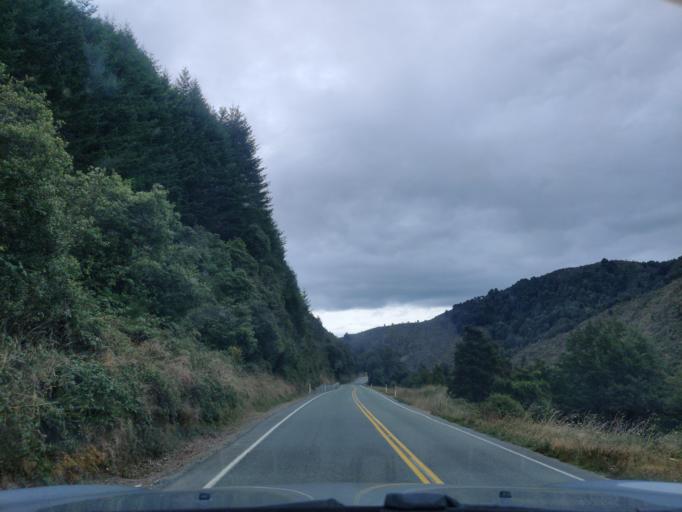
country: NZ
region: Tasman
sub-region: Tasman District
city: Wakefield
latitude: -41.7014
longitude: 172.6450
